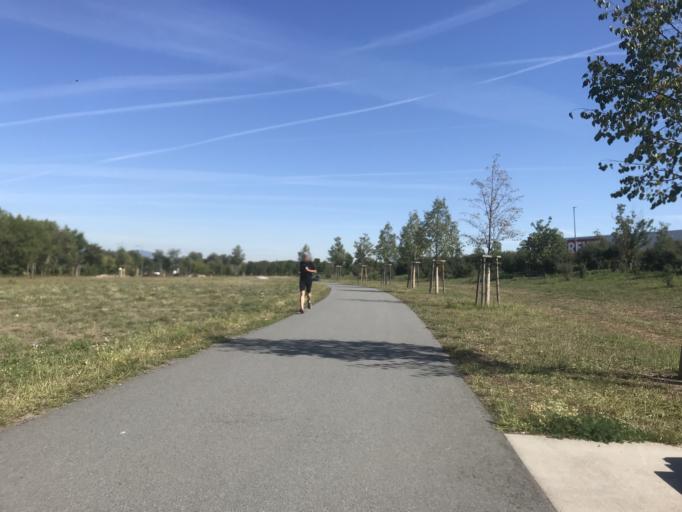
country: DE
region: Hesse
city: Raunheim
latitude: 50.0319
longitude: 8.4722
